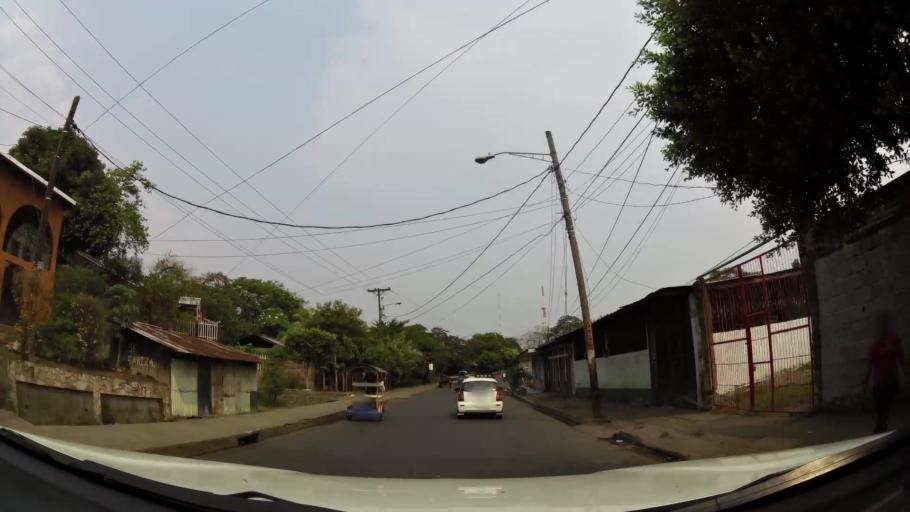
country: NI
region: Chinandega
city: Chinandega
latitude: 12.6354
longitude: -87.1361
